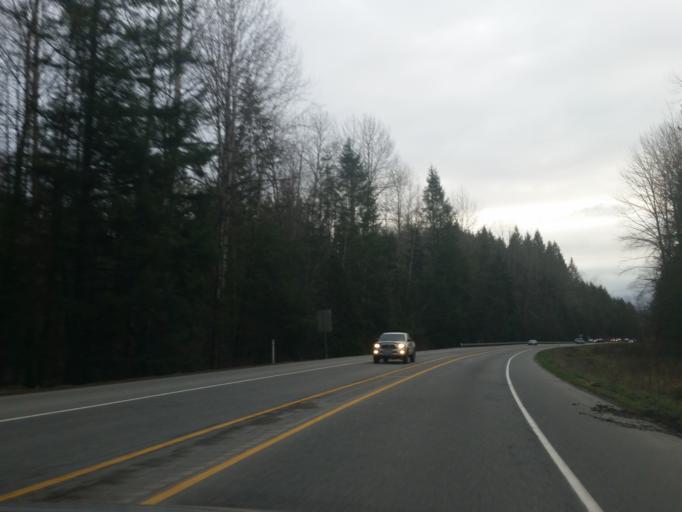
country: US
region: Washington
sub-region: Snohomish County
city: Maltby
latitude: 47.8125
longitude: -122.0956
